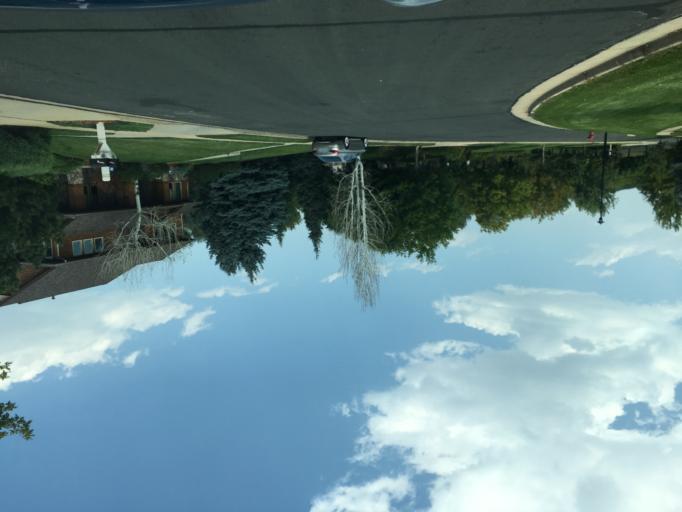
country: US
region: Colorado
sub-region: Boulder County
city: Lafayette
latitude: 40.0155
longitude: -105.1202
